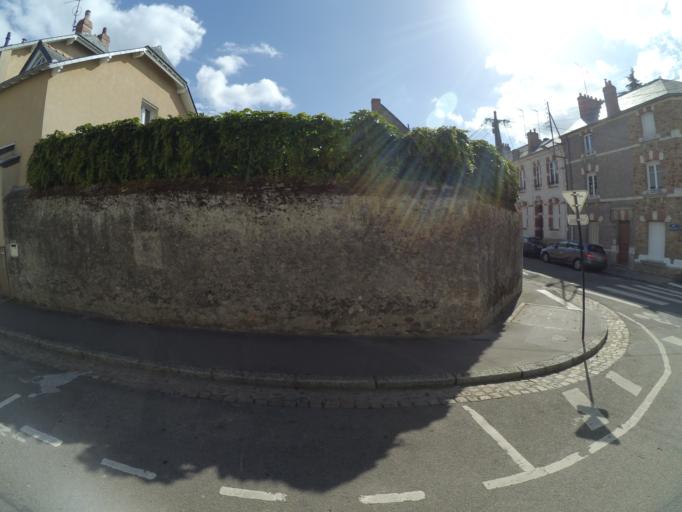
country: FR
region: Pays de la Loire
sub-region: Departement de la Loire-Atlantique
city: Nantes
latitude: 47.2269
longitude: -1.5632
